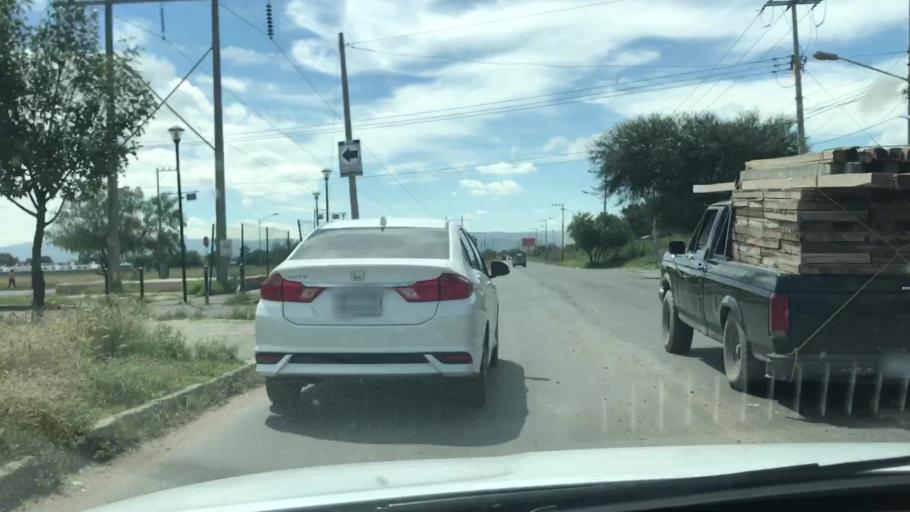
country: MX
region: Guanajuato
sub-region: Celaya
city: La Trinidad
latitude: 20.5442
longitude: -100.7802
